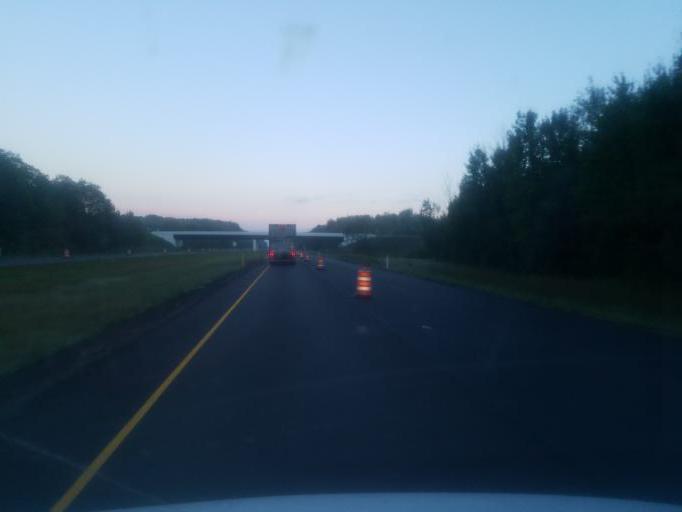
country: US
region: Ohio
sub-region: Ashtabula County
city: Jefferson
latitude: 41.7839
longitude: -80.7340
